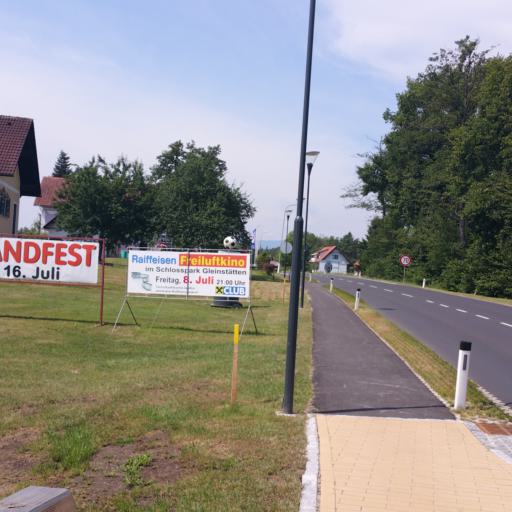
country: AT
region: Styria
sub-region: Politischer Bezirk Leibnitz
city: Gleinstatten
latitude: 46.7531
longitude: 15.3601
